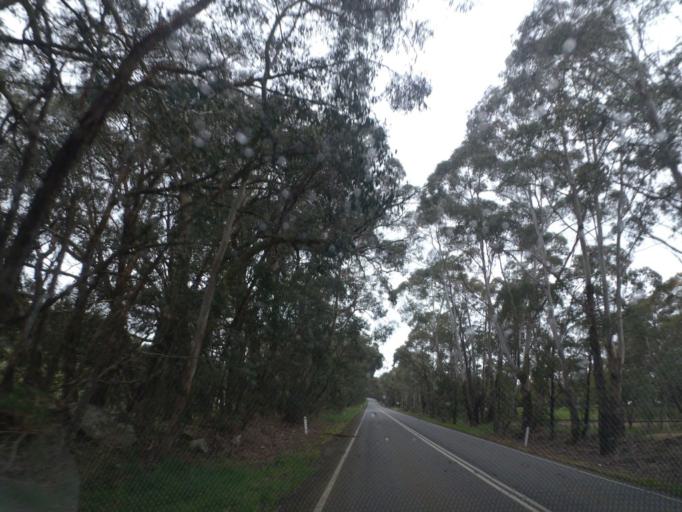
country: AU
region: Victoria
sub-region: Hume
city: Sunbury
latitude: -37.3449
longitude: 144.6809
